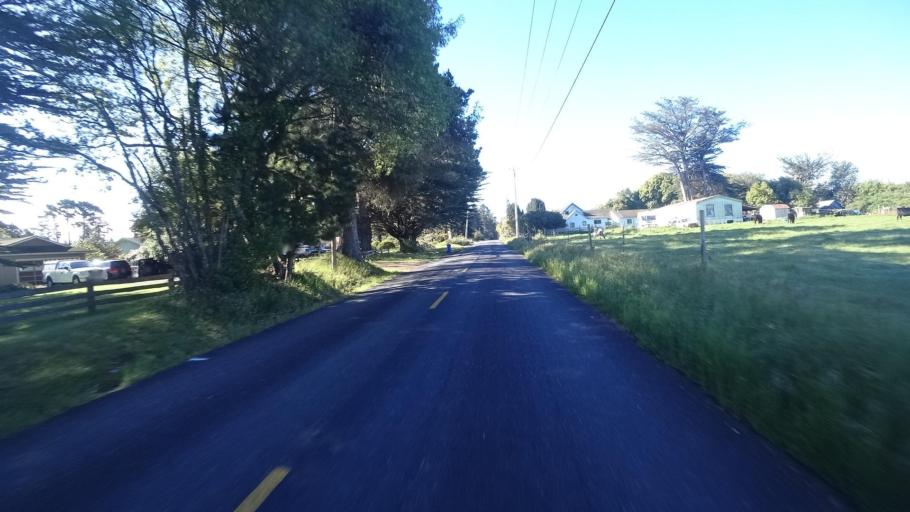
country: US
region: California
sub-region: Humboldt County
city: McKinleyville
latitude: 40.9908
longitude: -124.1005
